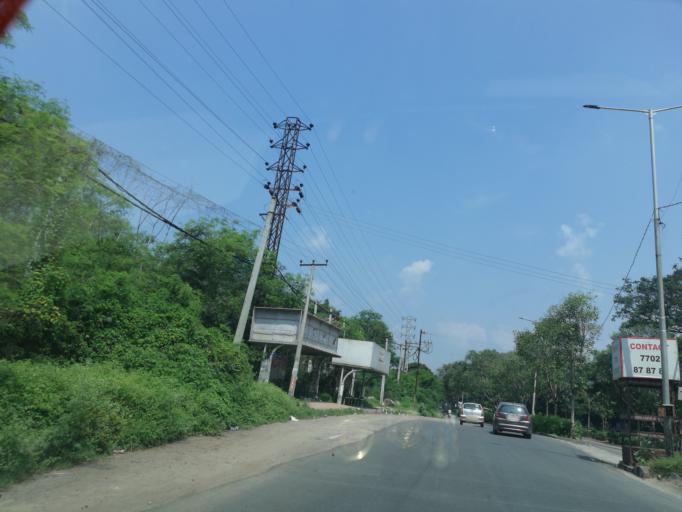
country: IN
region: Telangana
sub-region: Medak
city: Serilingampalle
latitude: 17.4600
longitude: 78.3375
